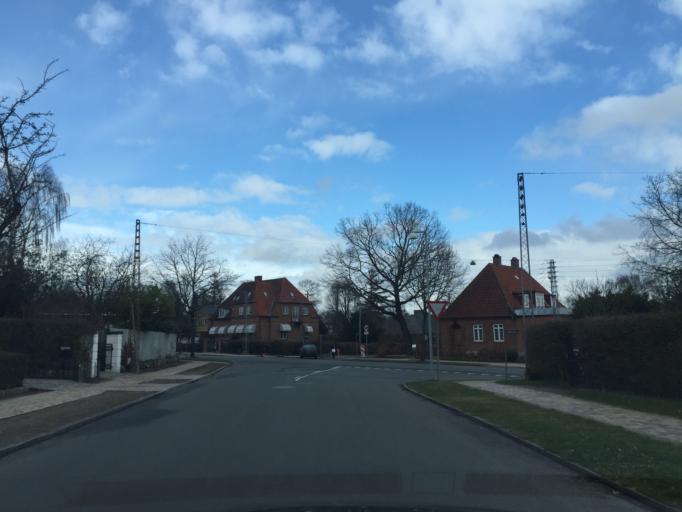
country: DK
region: South Denmark
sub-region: Odense Kommune
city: Odense
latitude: 55.3789
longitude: 10.3884
